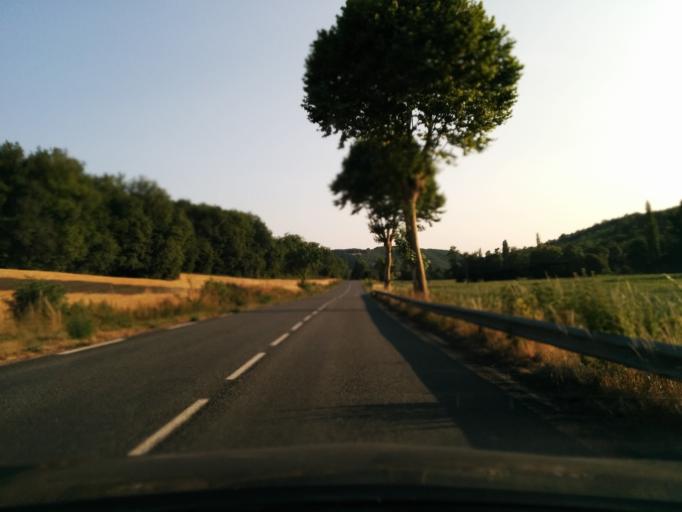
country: FR
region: Midi-Pyrenees
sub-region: Departement du Lot
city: Le Vigan
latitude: 44.6848
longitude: 1.4857
